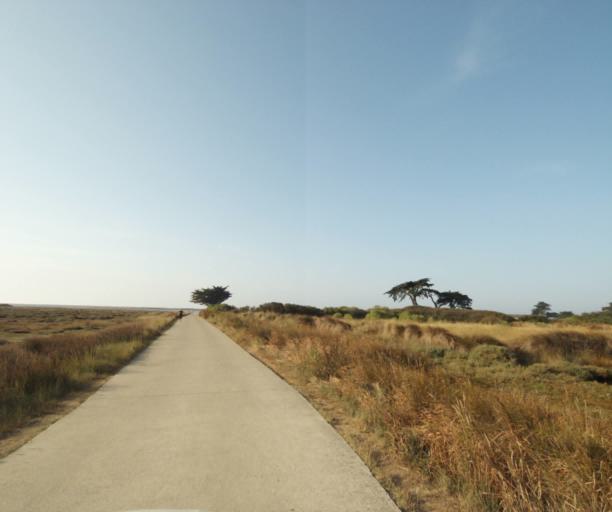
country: FR
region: Brittany
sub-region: Departement du Morbihan
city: Riantec
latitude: 47.7053
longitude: -3.3127
